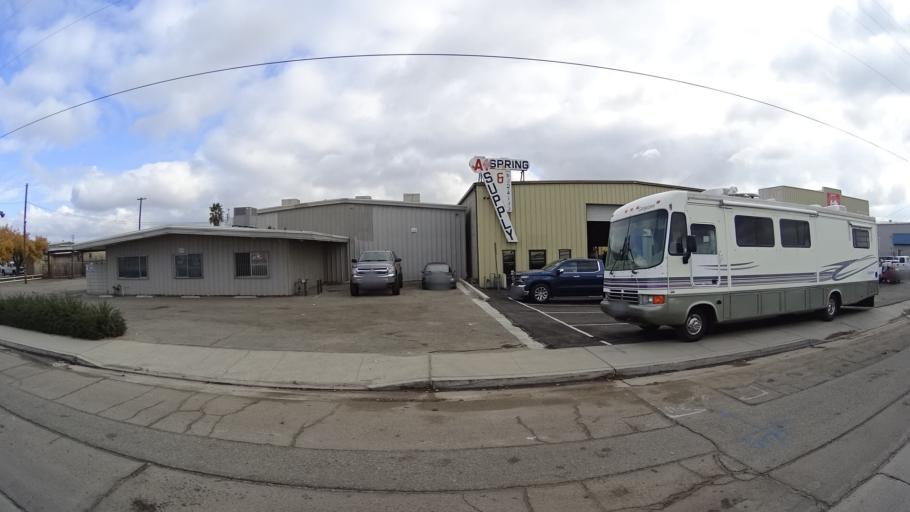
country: US
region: California
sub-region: Kern County
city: Bakersfield
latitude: 35.3344
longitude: -119.0030
